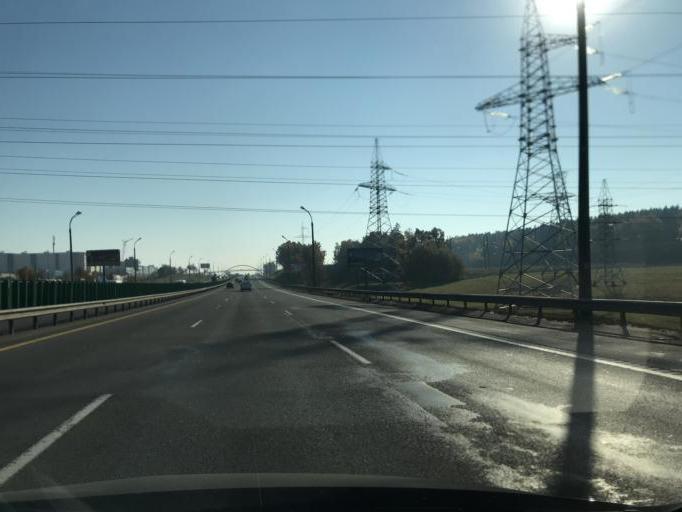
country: BY
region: Minsk
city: Malinovka
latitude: 53.8695
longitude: 27.4227
